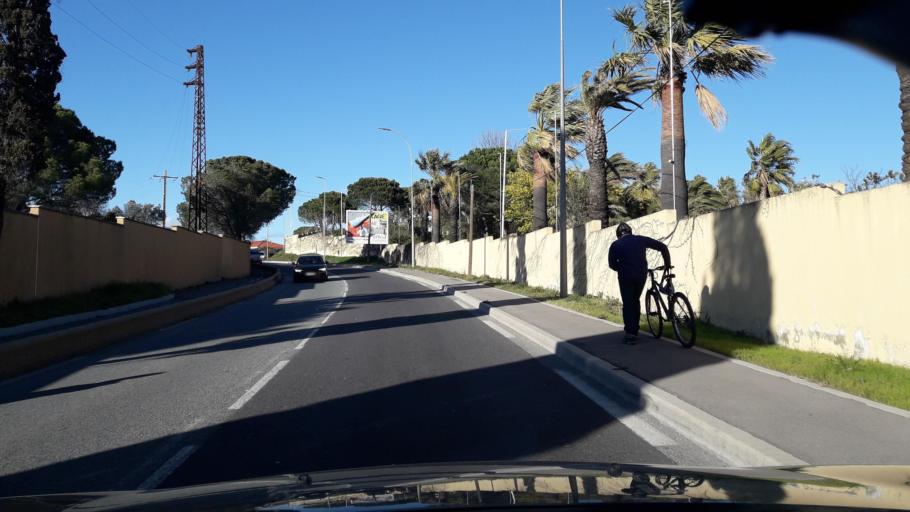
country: FR
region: Provence-Alpes-Cote d'Azur
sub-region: Departement du Var
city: Frejus
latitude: 43.4464
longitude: 6.7270
